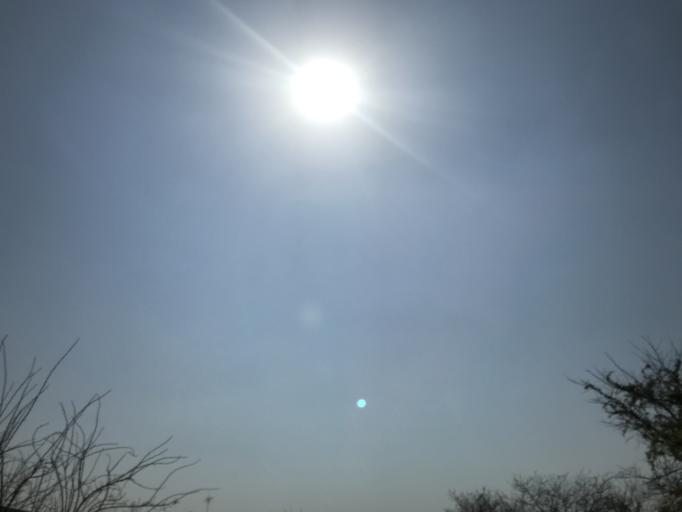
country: JP
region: Ibaraki
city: Moriya
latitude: 35.9288
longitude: 139.9710
